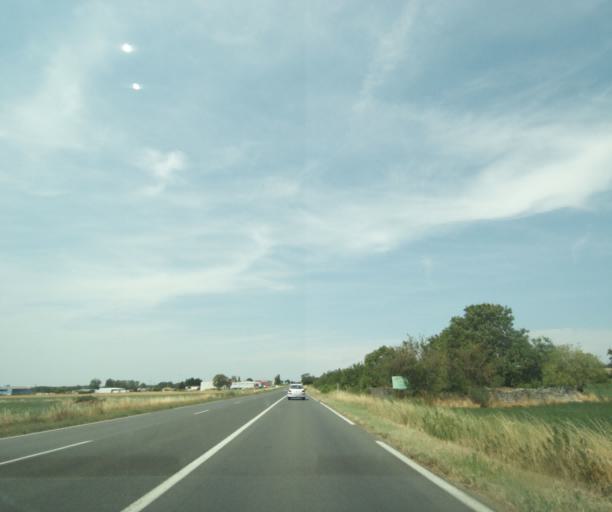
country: FR
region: Poitou-Charentes
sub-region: Departement de la Vienne
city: Les Ormes
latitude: 46.9563
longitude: 0.6076
